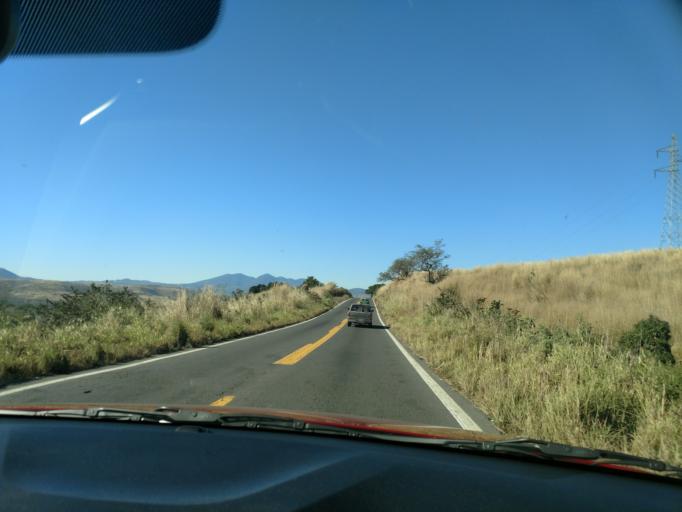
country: MX
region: Nayarit
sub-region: Ahuacatlan
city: Ahuacatlan
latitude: 21.1182
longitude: -104.5920
